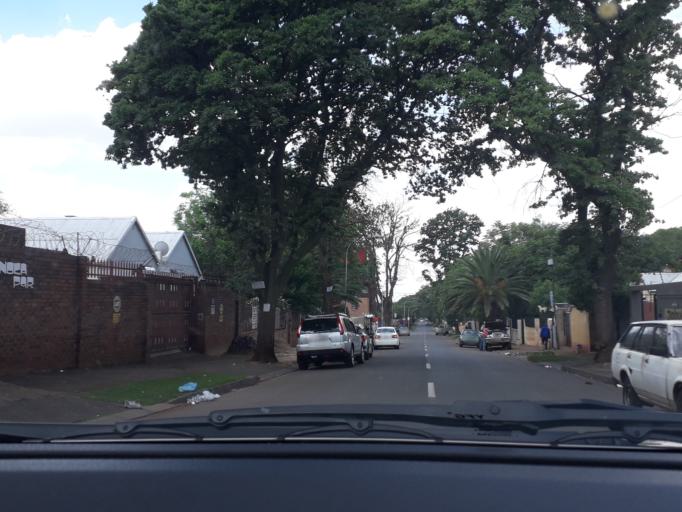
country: ZA
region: Gauteng
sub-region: City of Johannesburg Metropolitan Municipality
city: Johannesburg
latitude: -26.1798
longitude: 28.0705
